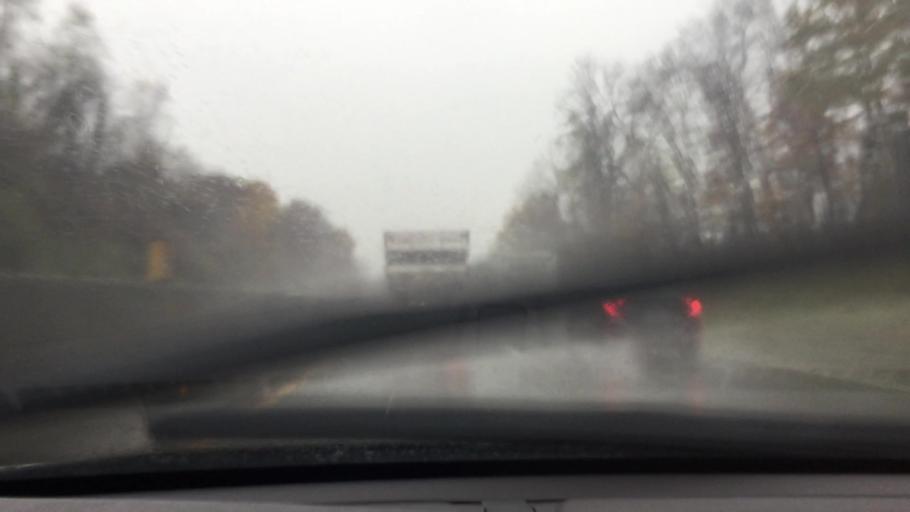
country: US
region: Pennsylvania
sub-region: Washington County
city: Ellsworth
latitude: 40.1652
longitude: -80.0738
